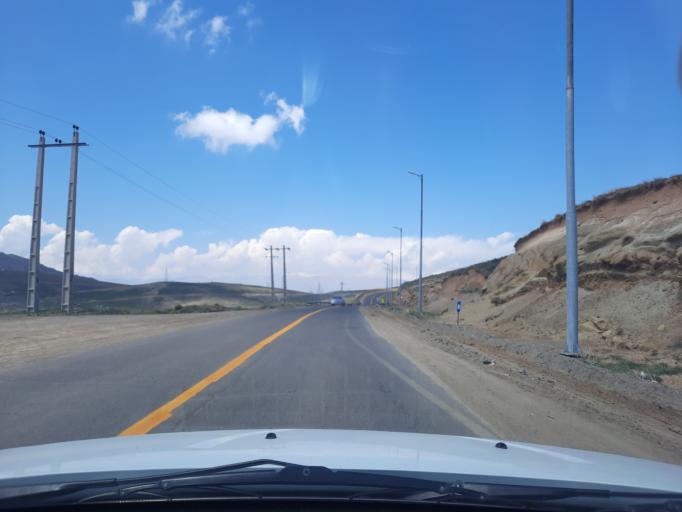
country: IR
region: Qazvin
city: Qazvin
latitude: 36.3854
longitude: 50.2068
